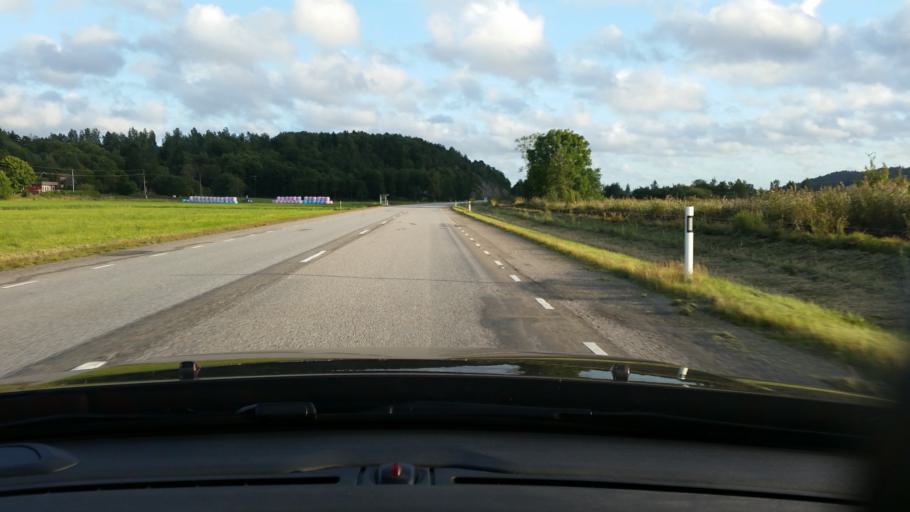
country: SE
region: Vaestra Goetaland
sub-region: Lilla Edets Kommun
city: Lodose
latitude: 58.0471
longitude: 12.1504
